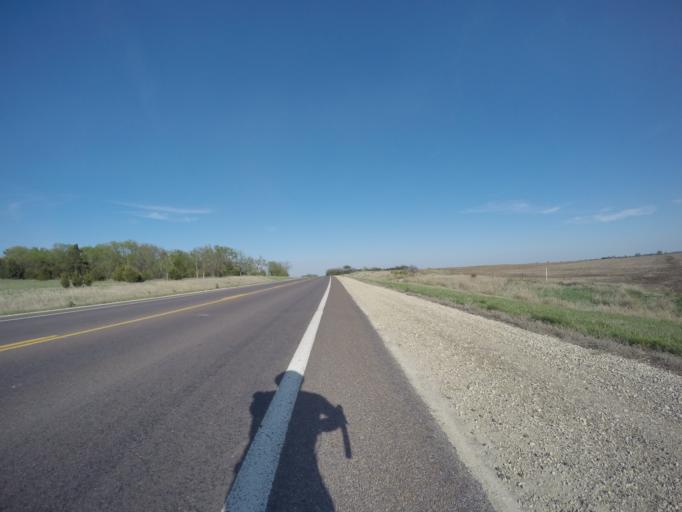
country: US
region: Kansas
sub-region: Riley County
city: Fort Riley North
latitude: 39.2985
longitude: -96.7895
